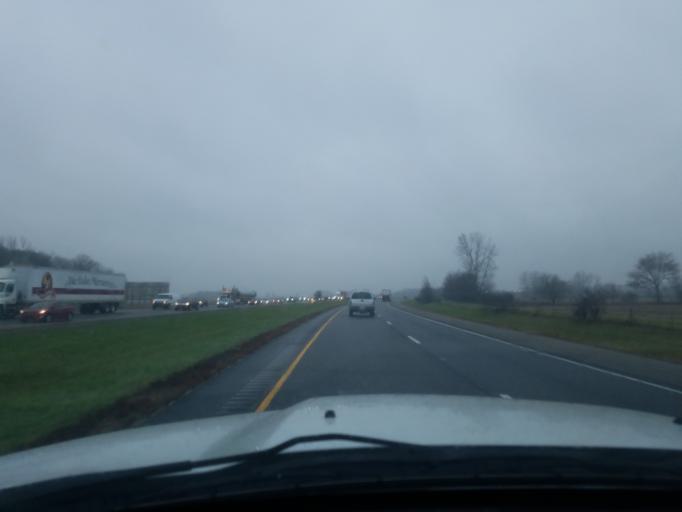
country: US
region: Indiana
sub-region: Grant County
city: Upland
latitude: 40.3873
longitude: -85.5486
